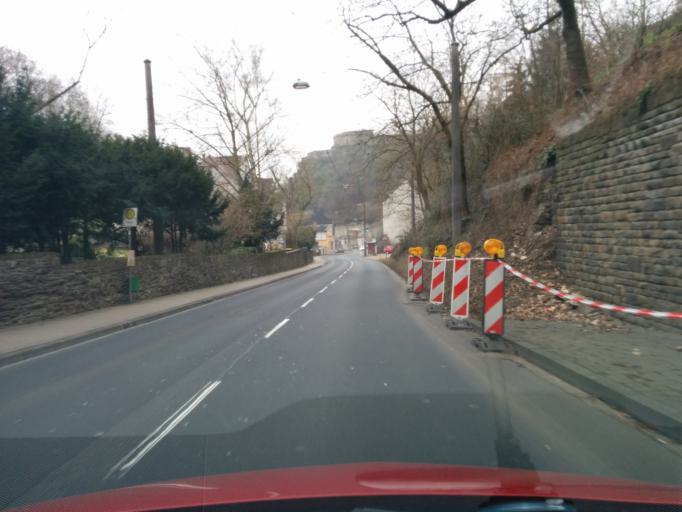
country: DE
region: Rheinland-Pfalz
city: Urbar
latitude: 50.3632
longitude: 7.6177
